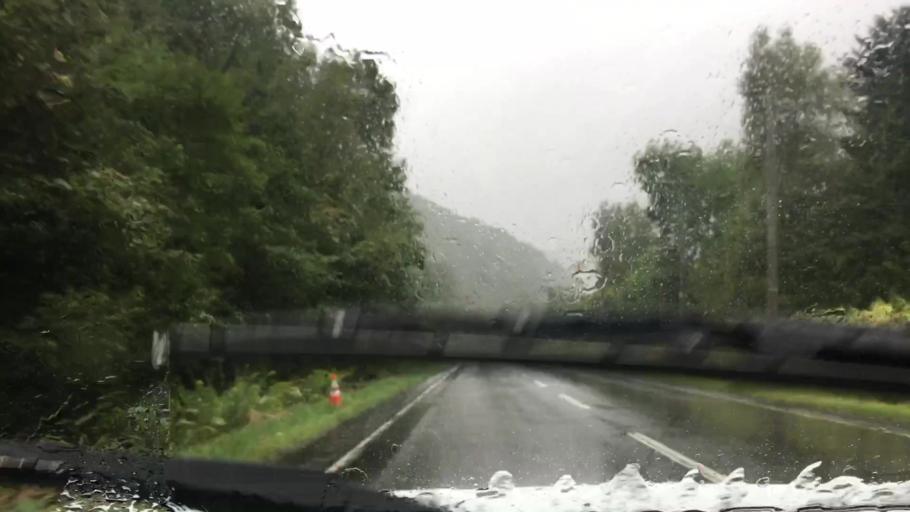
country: JP
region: Hokkaido
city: Sapporo
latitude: 42.9490
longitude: 141.1457
